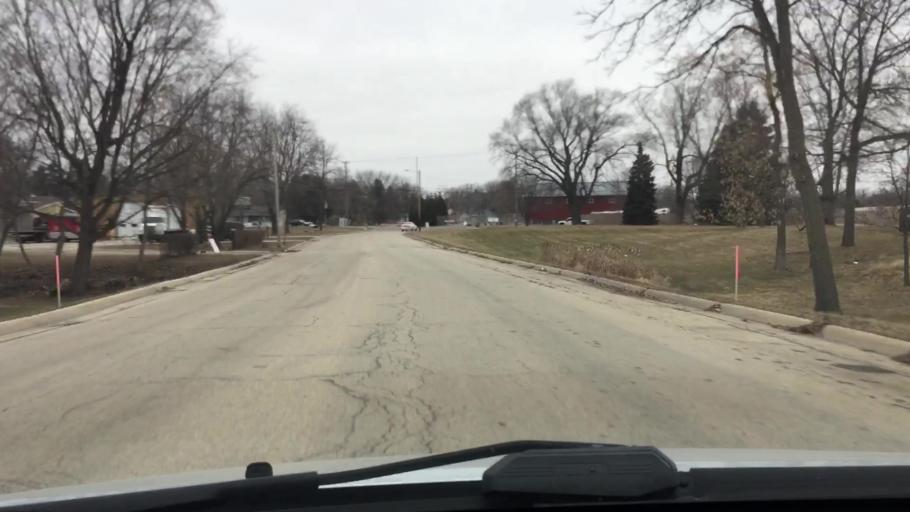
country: US
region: Wisconsin
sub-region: Jefferson County
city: Watertown
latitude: 43.1879
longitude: -88.7335
